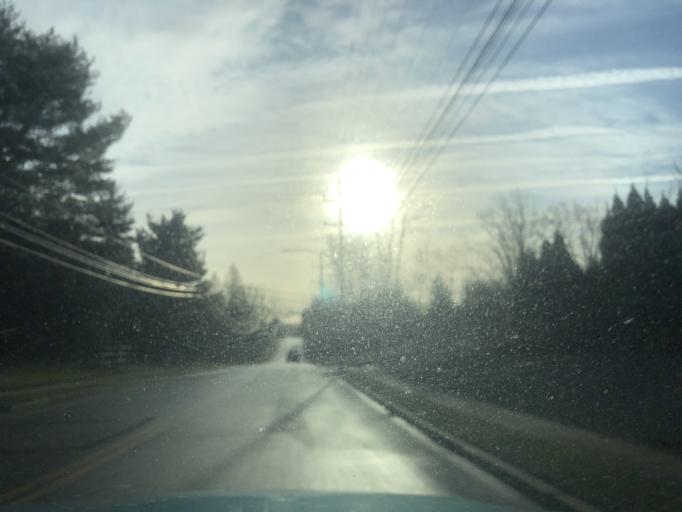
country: US
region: Pennsylvania
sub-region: Montgomery County
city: Fort Washington
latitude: 40.1458
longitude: -75.2000
